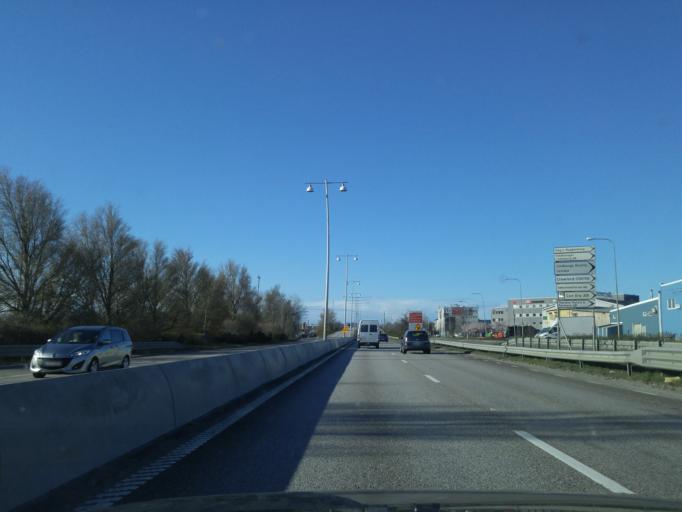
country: SE
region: Vaestra Goetaland
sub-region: Goteborg
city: Goeteborg
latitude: 57.7340
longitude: 12.0016
